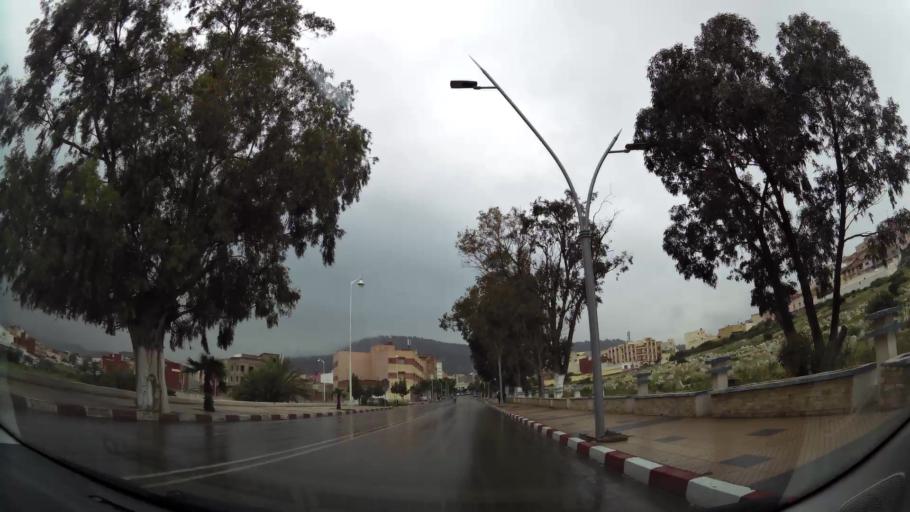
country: MA
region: Oriental
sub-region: Nador
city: Nador
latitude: 35.1539
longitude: -2.9956
